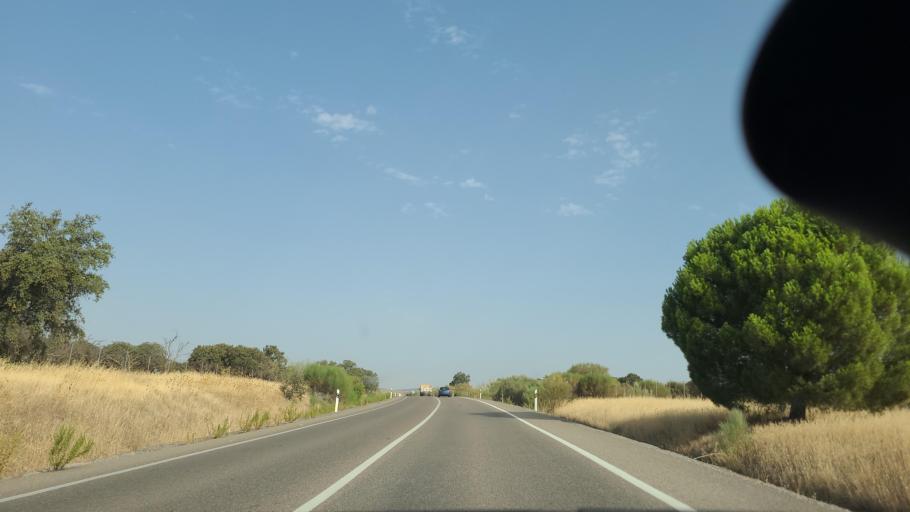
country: ES
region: Andalusia
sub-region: Province of Cordoba
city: Belmez
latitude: 38.2544
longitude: -5.1693
